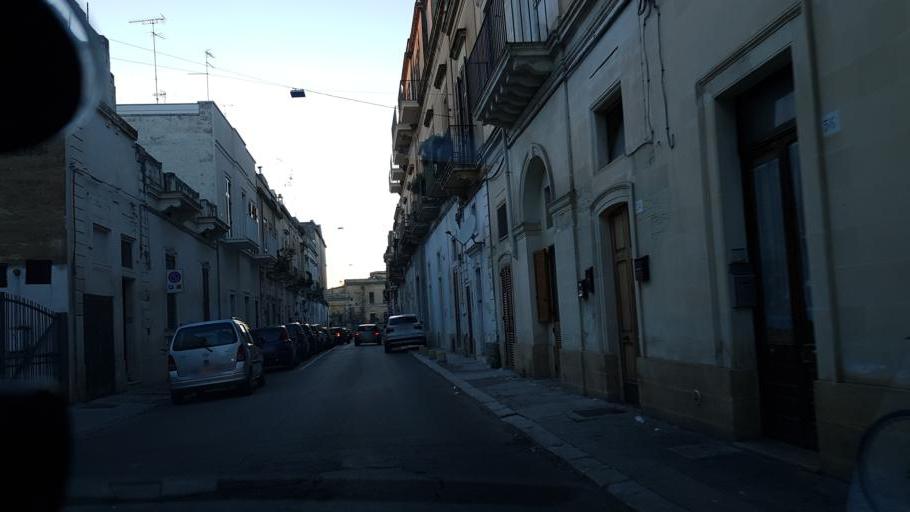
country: IT
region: Apulia
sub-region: Provincia di Lecce
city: Lecce
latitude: 40.3569
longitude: 18.1761
